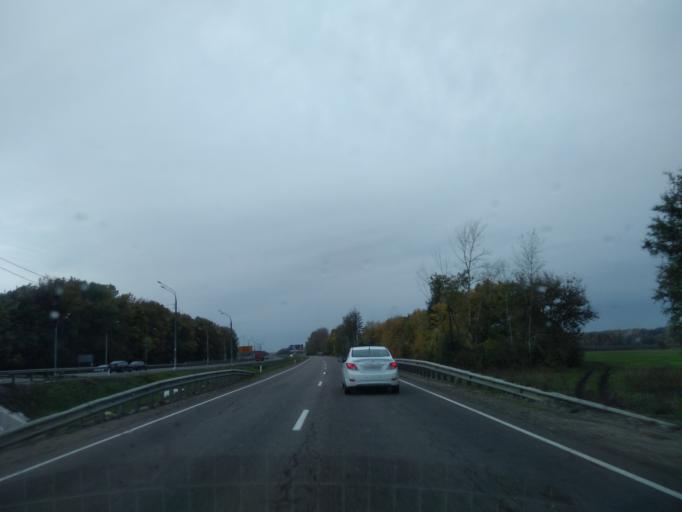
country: RU
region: Lipetsk
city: Zadonsk
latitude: 52.4401
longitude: 38.8060
